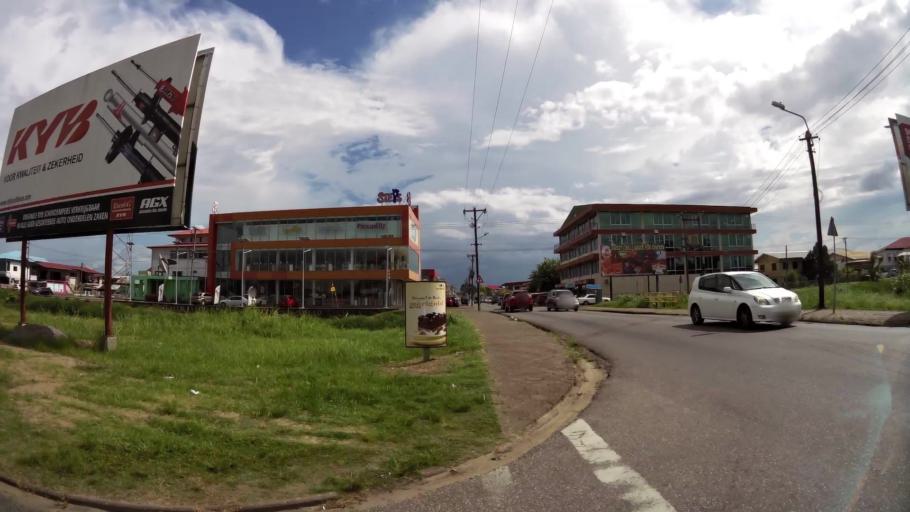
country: SR
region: Paramaribo
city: Paramaribo
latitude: 5.8429
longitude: -55.1434
